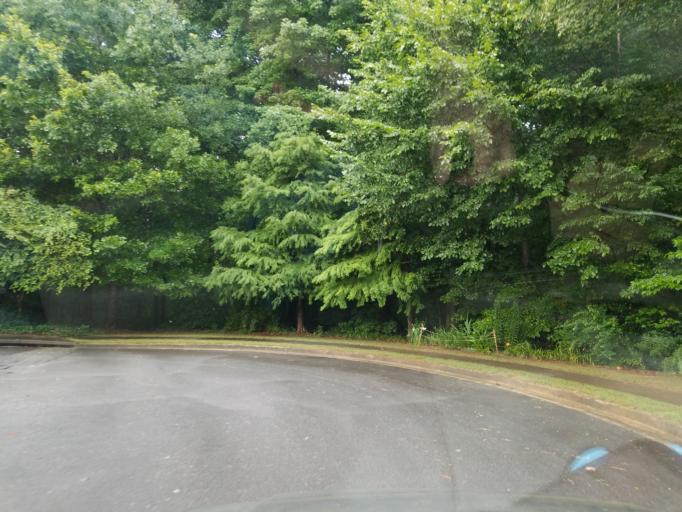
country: US
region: Georgia
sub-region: Cherokee County
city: Woodstock
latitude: 34.0548
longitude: -84.4865
